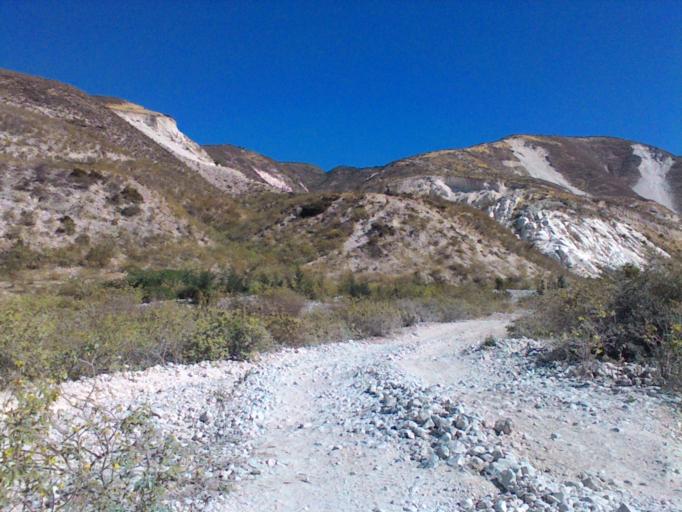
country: HT
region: Ouest
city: Croix des Bouquets
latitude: 18.6788
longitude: -72.2347
